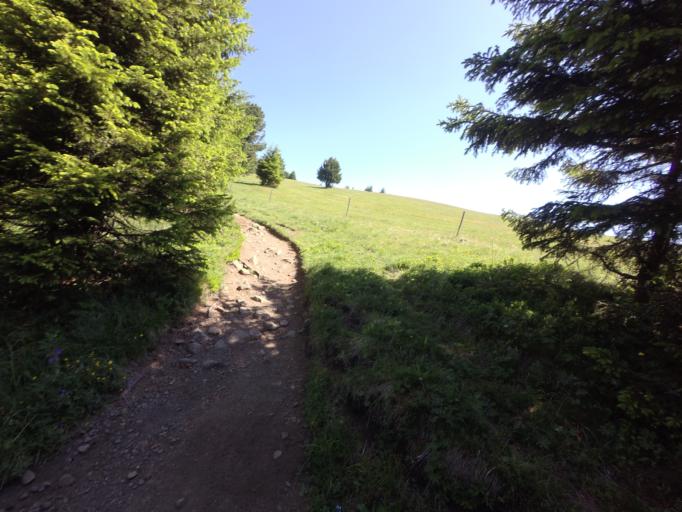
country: IT
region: Trentino-Alto Adige
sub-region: Bolzano
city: Castelrotto
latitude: 46.5561
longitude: 11.5991
